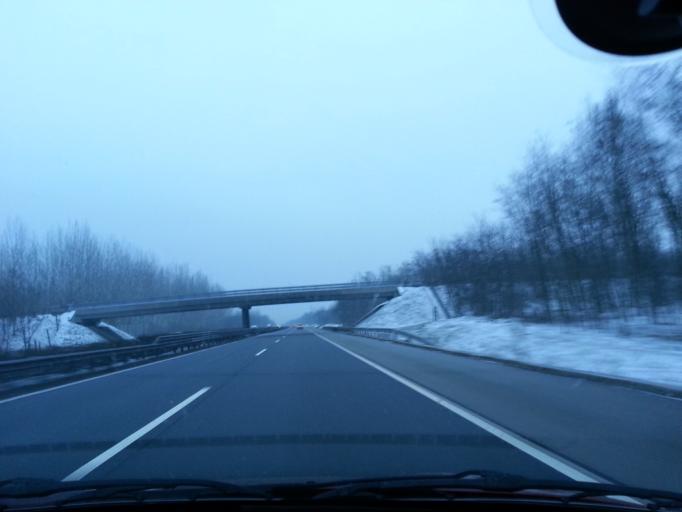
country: HU
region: Pest
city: Inarcs
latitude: 47.2928
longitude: 19.2986
